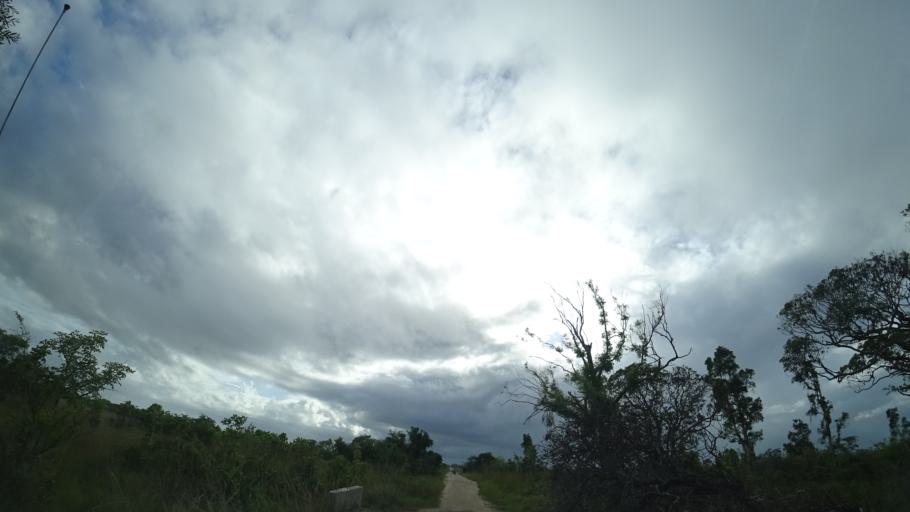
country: MZ
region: Sofala
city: Beira
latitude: -19.6912
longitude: 35.0408
